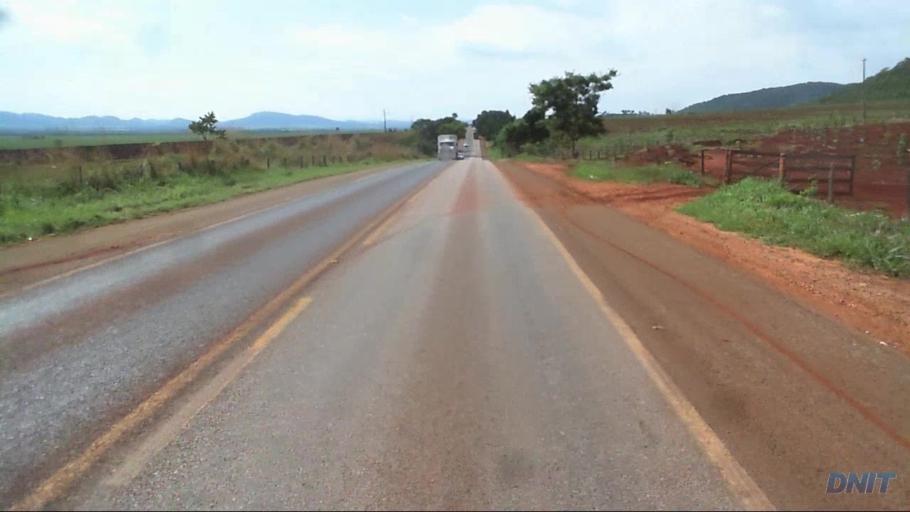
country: BR
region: Goias
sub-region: Barro Alto
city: Barro Alto
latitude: -14.9954
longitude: -48.9068
